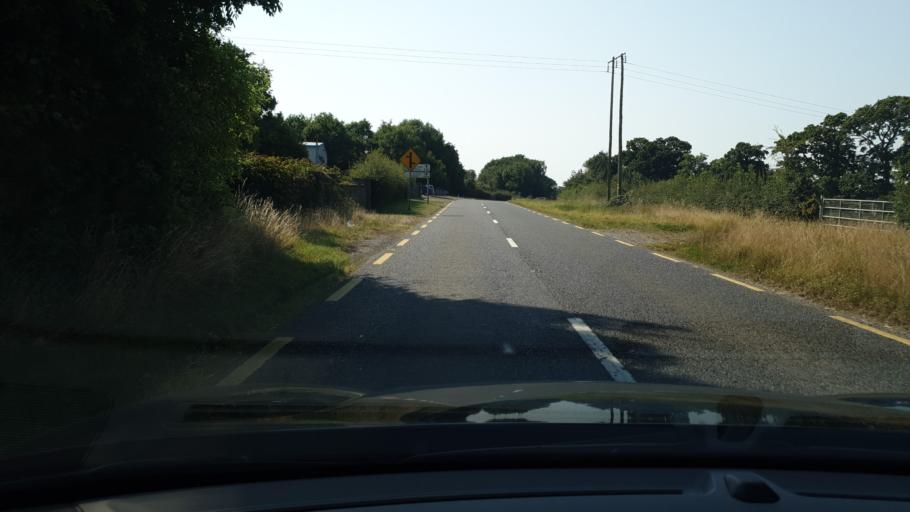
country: IE
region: Leinster
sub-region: Kildare
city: Kilcock
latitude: 53.4783
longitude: -6.7120
